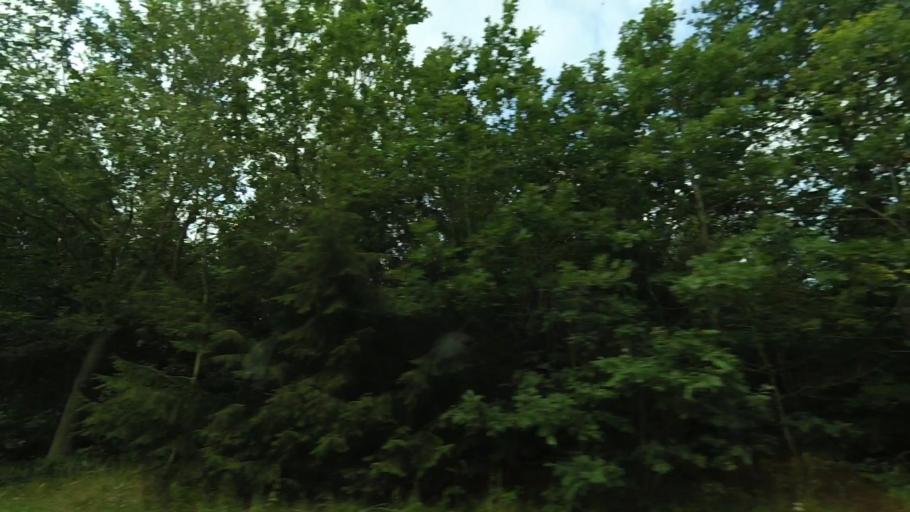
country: DK
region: Central Jutland
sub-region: Syddjurs Kommune
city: Ryomgard
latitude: 56.4171
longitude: 10.5601
